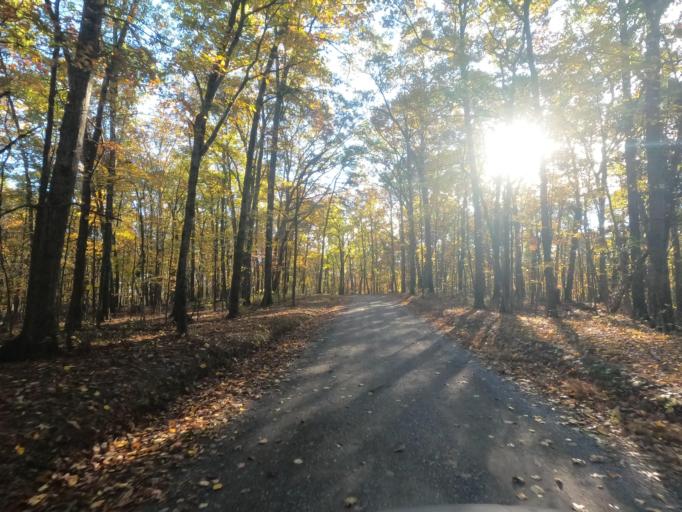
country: US
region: West Virginia
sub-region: Morgan County
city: Berkeley Springs
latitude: 39.6561
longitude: -78.4594
